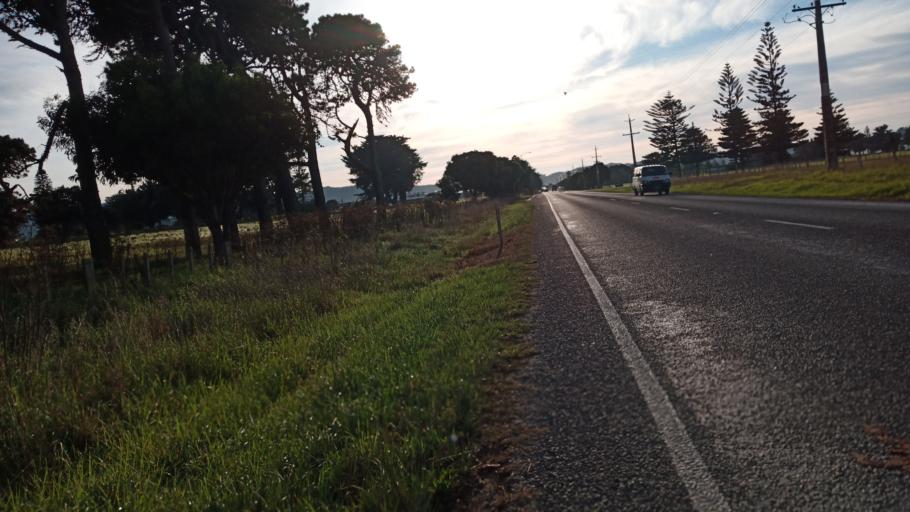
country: NZ
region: Gisborne
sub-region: Gisborne District
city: Gisborne
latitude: -38.6717
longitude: 177.9904
